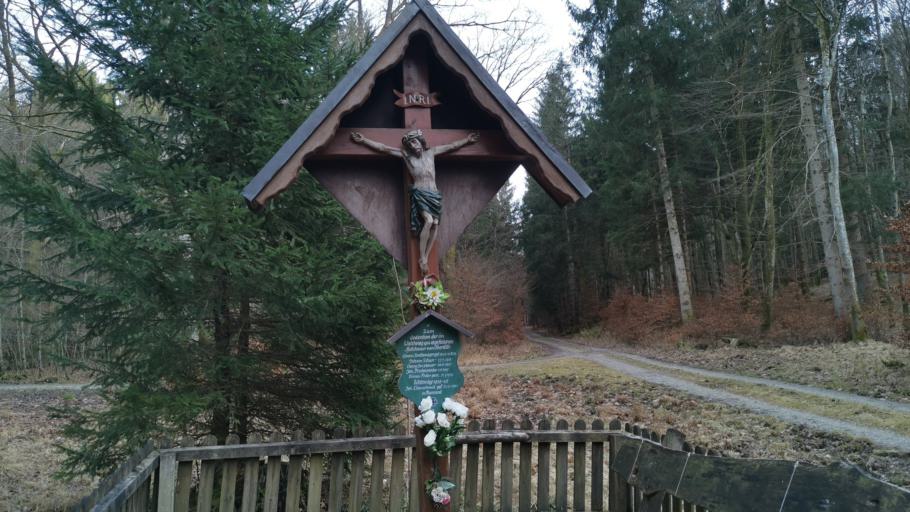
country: DE
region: Bavaria
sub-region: Upper Bavaria
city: Schaftlarn
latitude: 48.0258
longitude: 11.4377
